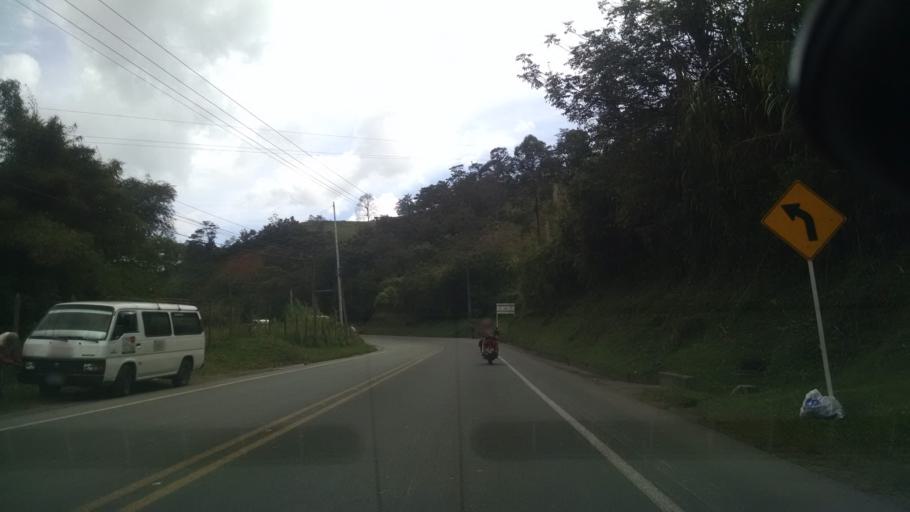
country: CO
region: Antioquia
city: Caldas
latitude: 6.0647
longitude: -75.6335
